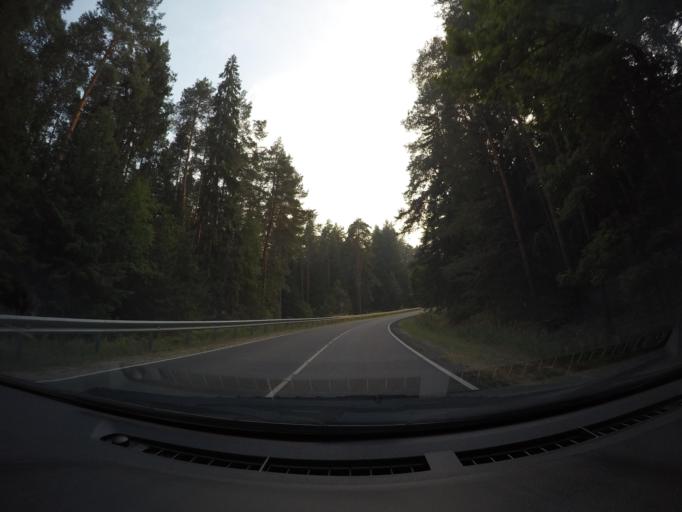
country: RU
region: Moskovskaya
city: Imeni Tsyurupy
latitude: 55.5039
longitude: 38.7135
